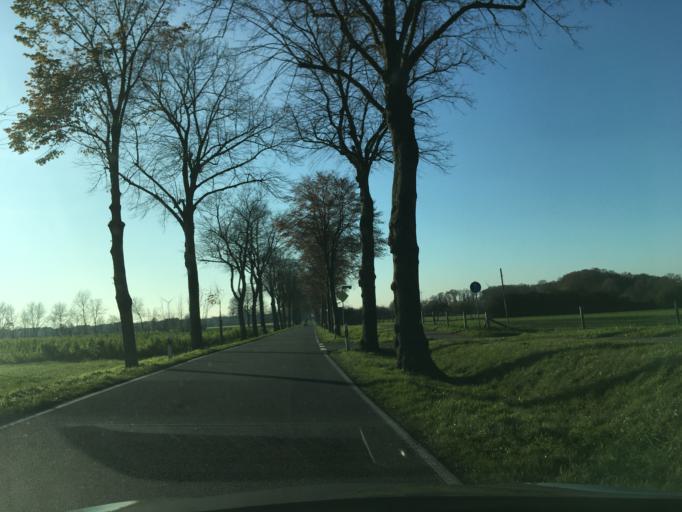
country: DE
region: North Rhine-Westphalia
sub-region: Regierungsbezirk Munster
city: Vreden
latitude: 52.1052
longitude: 6.8695
